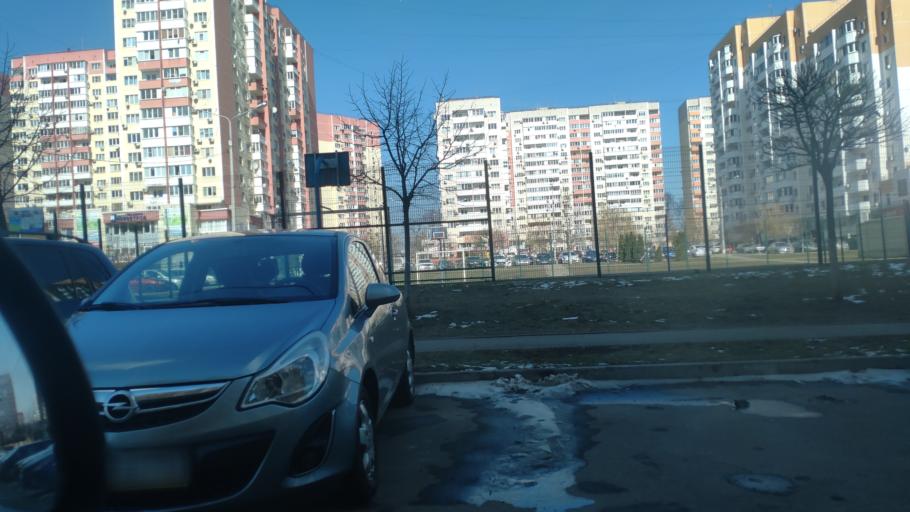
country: RU
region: Krasnodarskiy
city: Krasnodar
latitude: 45.0587
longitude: 39.0286
